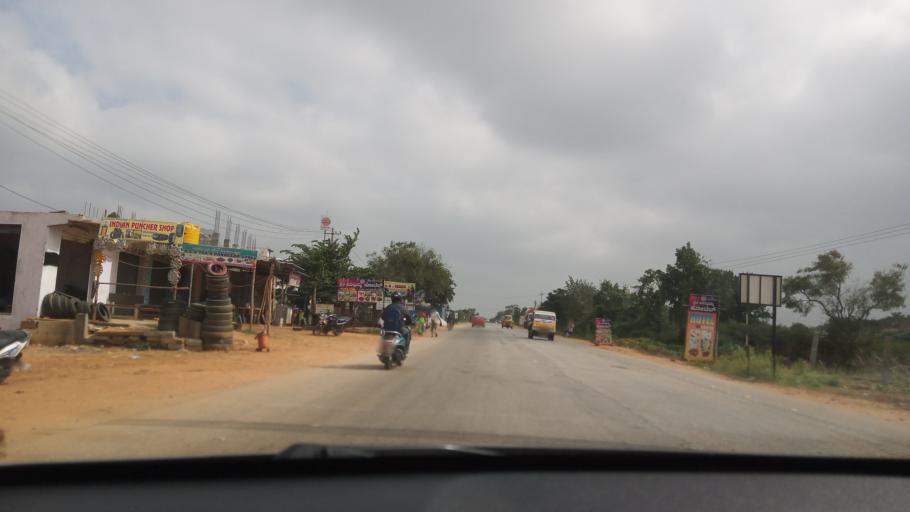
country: IN
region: Karnataka
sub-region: Chikkaballapur
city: Chintamani
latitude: 13.3275
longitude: 77.9931
